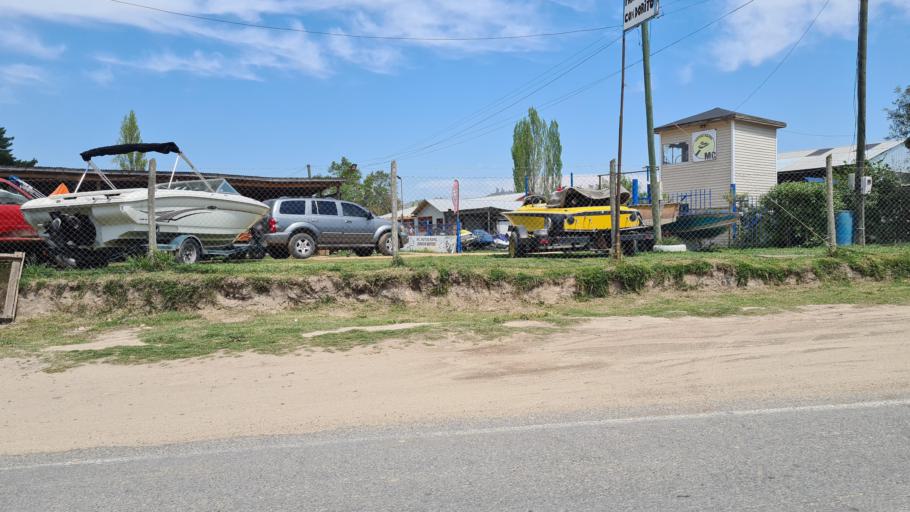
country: CL
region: O'Higgins
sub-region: Provincia de Cachapoal
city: San Vicente
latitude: -34.1578
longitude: -71.4449
